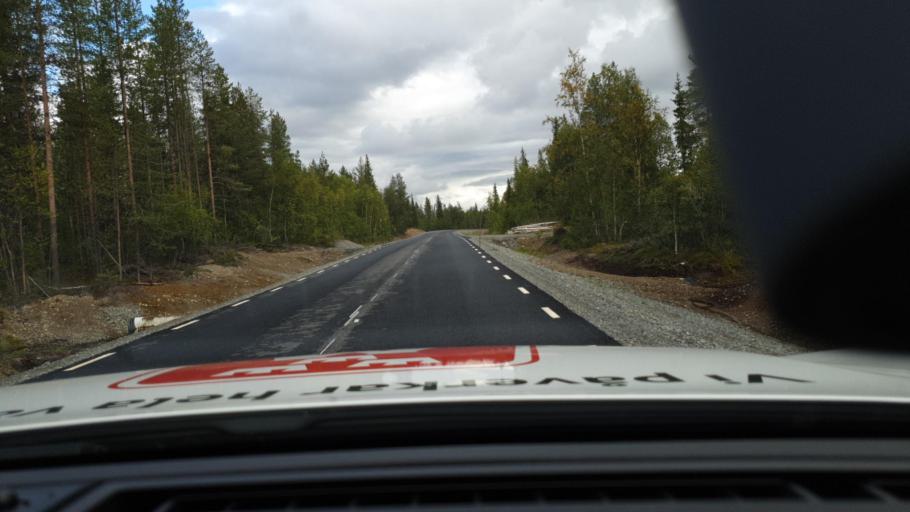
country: SE
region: Norrbotten
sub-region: Gallivare Kommun
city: Gaellivare
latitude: 66.8716
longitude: 21.2227
